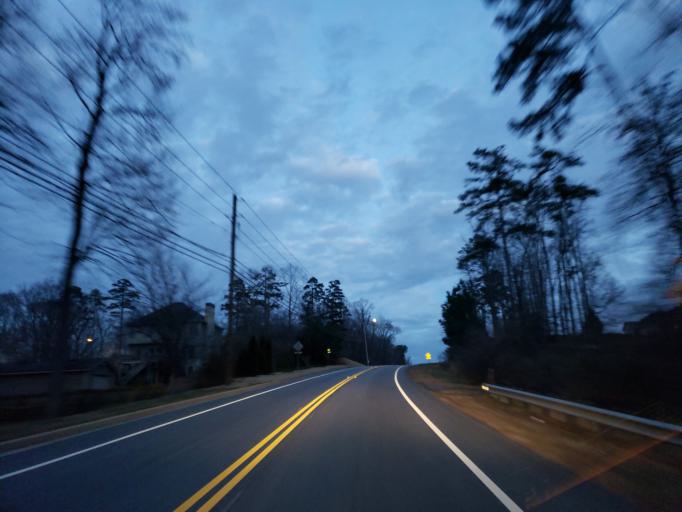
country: US
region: Georgia
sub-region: Cobb County
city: Kennesaw
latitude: 33.9995
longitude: -84.6686
